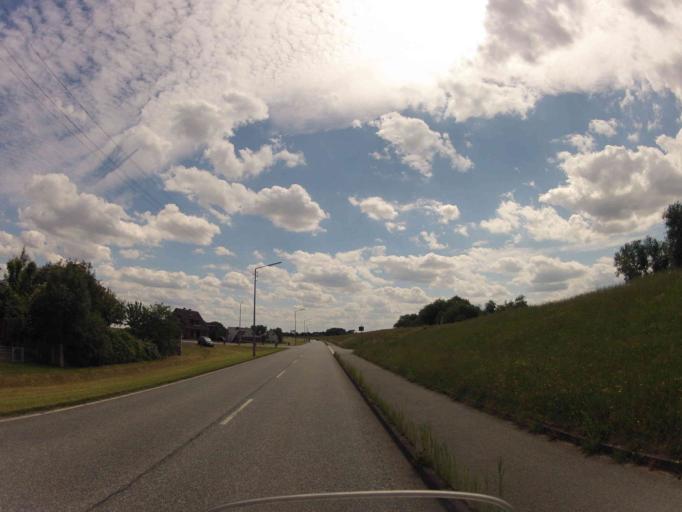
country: DE
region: Hamburg
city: Rothenburgsort
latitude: 53.4682
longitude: 10.0656
